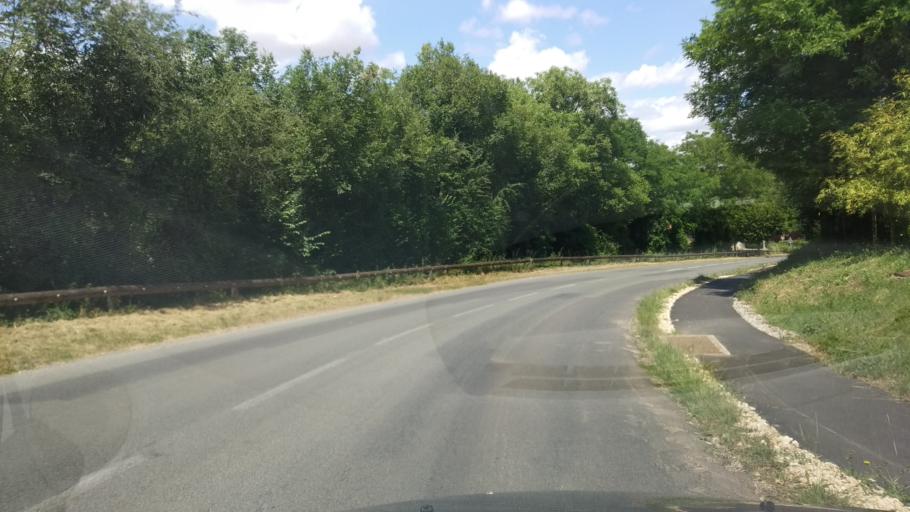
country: FR
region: Poitou-Charentes
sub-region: Departement de la Vienne
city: Vouneuil-sous-Biard
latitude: 46.6031
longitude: 0.2390
